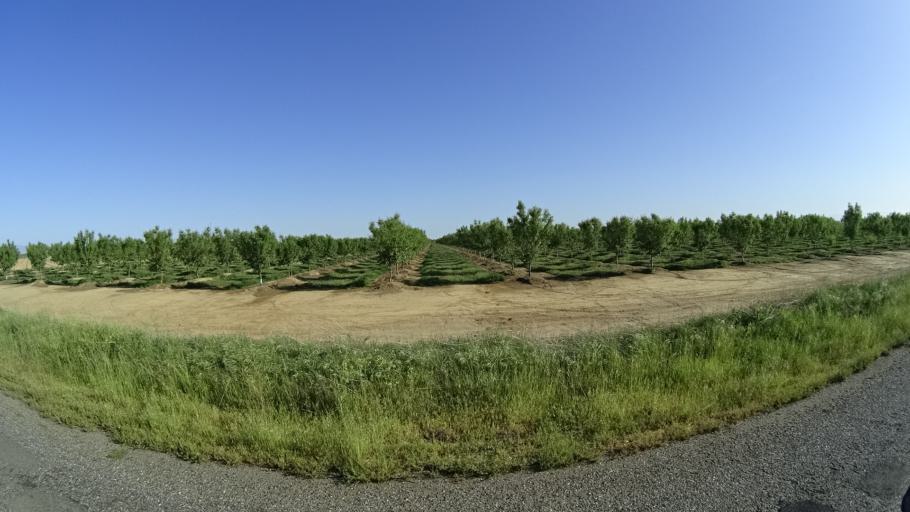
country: US
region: California
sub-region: Glenn County
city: Orland
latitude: 39.6816
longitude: -122.1445
